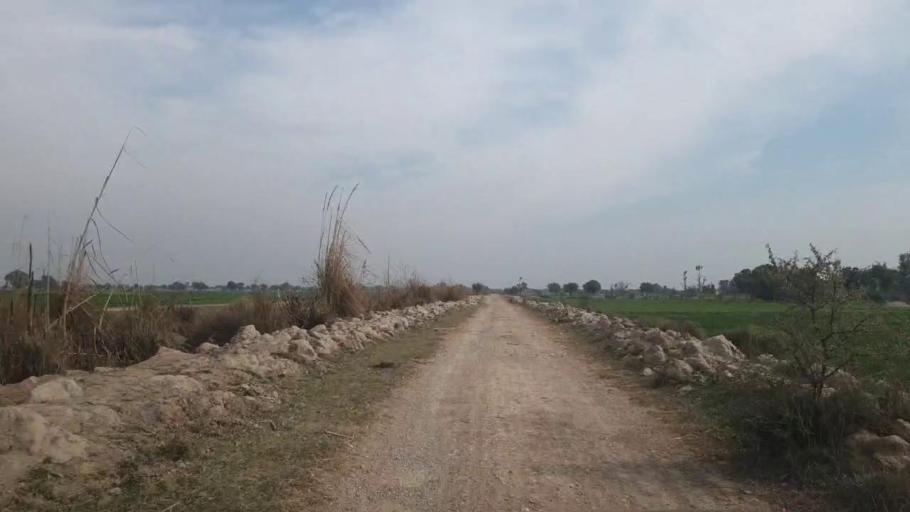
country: PK
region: Sindh
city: Nawabshah
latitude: 26.0754
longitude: 68.4555
